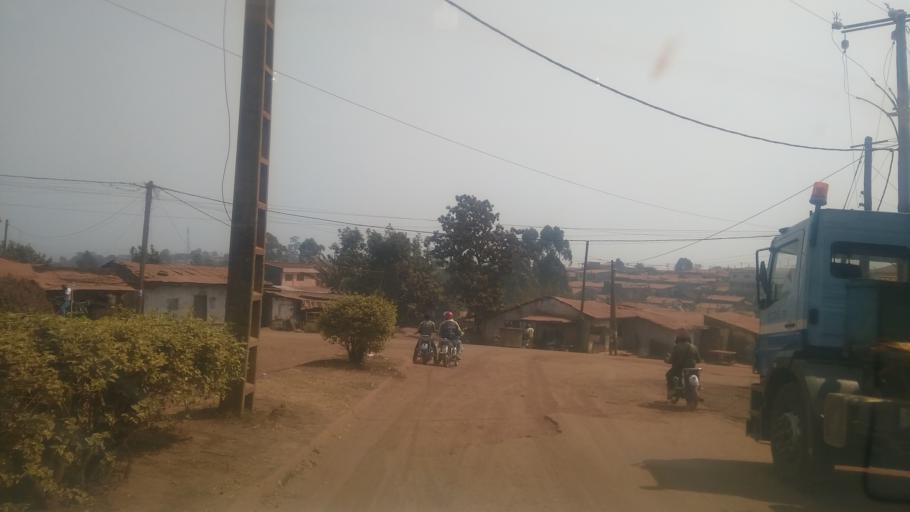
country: CM
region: West
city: Bafoussam
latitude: 5.4856
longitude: 10.4153
